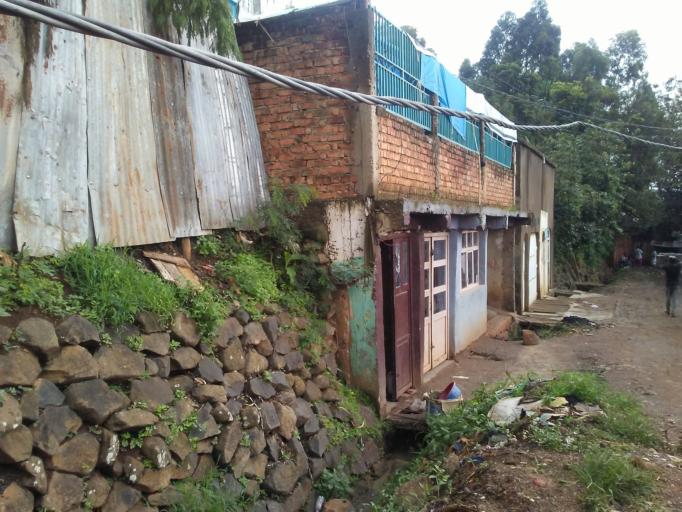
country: CD
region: South Kivu
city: Bukavu
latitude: -2.5124
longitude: 28.8495
